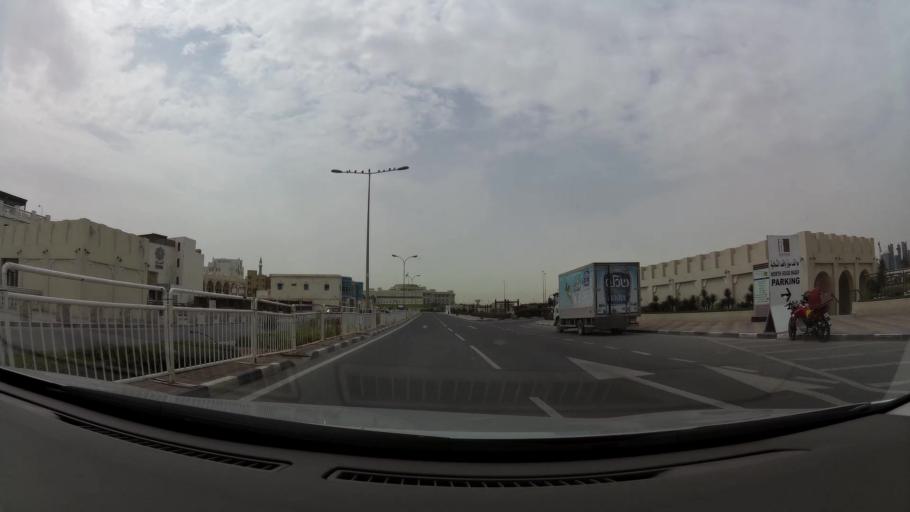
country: QA
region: Baladiyat ad Dawhah
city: Doha
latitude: 25.2900
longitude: 51.5334
